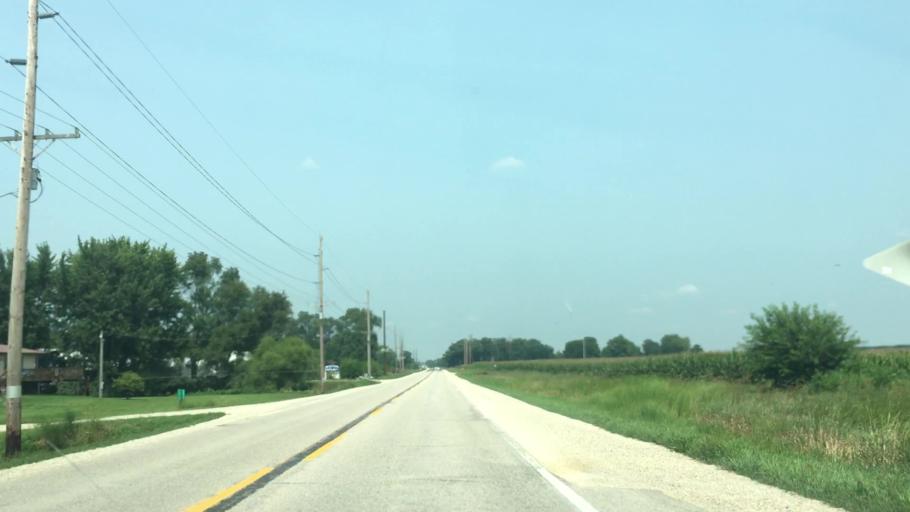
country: US
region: Iowa
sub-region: Buchanan County
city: Independence
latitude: 42.3739
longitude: -91.8894
